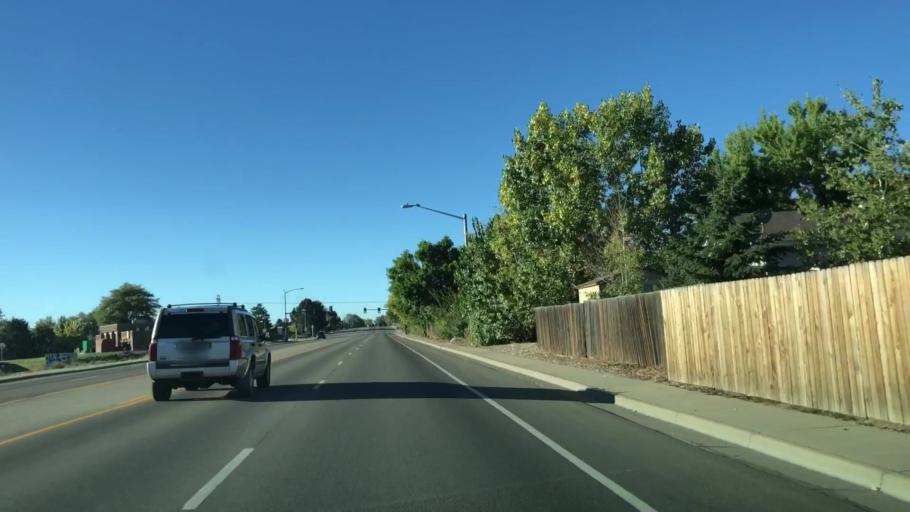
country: US
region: Colorado
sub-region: Larimer County
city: Loveland
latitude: 40.3848
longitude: -105.1160
